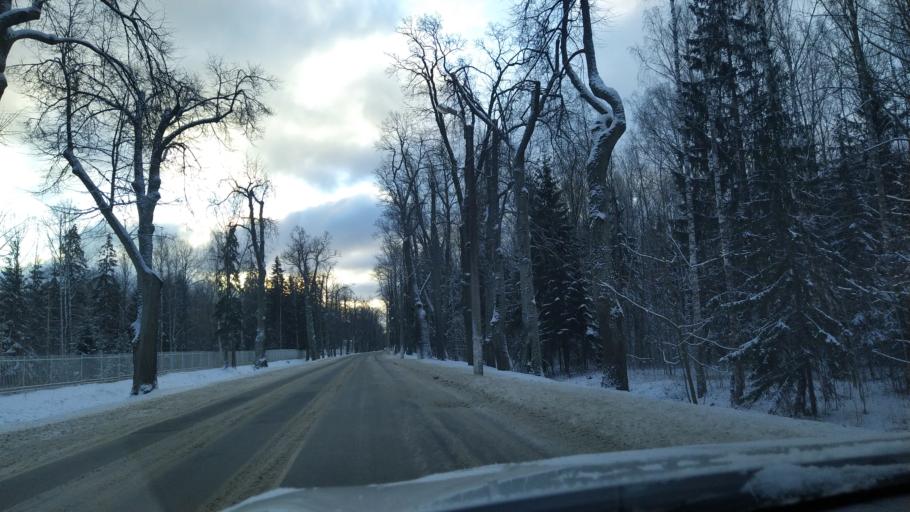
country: RU
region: St.-Petersburg
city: Aleksandrovskaya
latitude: 59.7233
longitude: 30.3624
